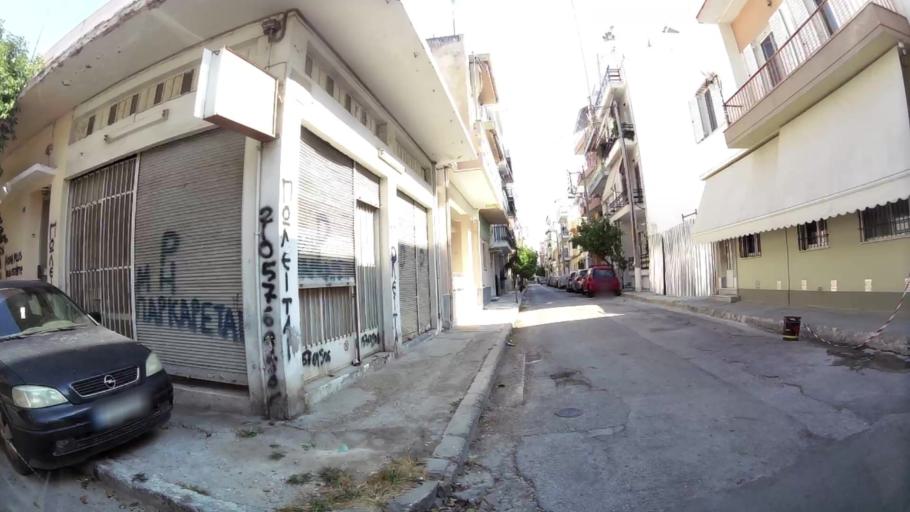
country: GR
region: Attica
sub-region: Nomos Piraios
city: Drapetsona
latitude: 37.9540
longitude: 23.6286
